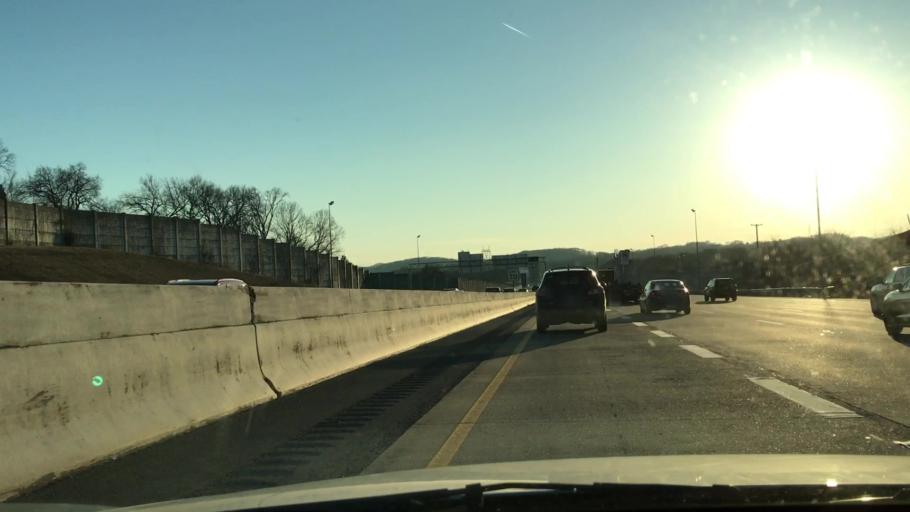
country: US
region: Tennessee
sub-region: Davidson County
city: Goodlettsville
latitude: 36.2967
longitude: -86.7148
